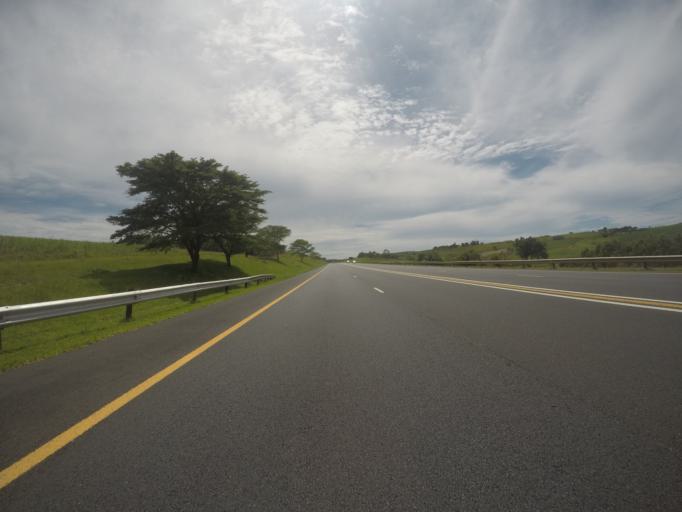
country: ZA
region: KwaZulu-Natal
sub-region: iLembe District Municipality
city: Mandeni
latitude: -29.1683
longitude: 31.5231
